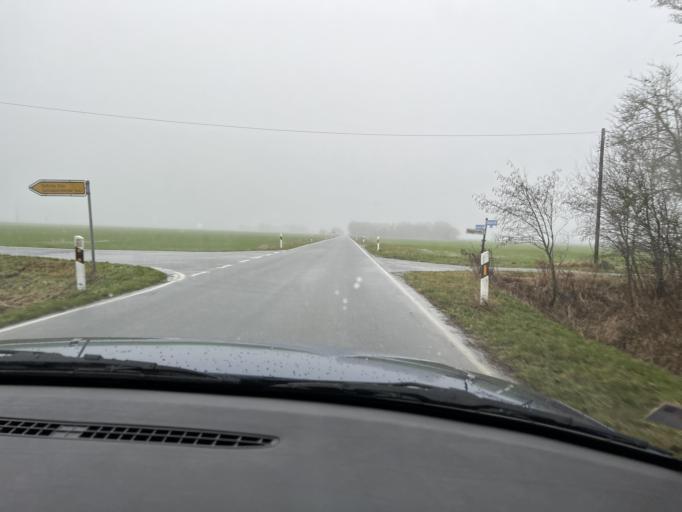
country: DE
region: Schleswig-Holstein
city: Schulp
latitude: 54.2565
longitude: 8.9109
